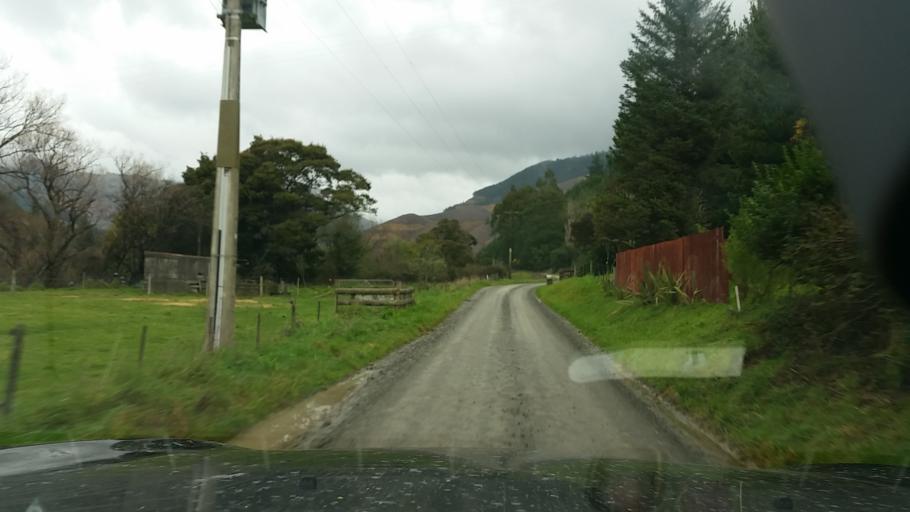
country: NZ
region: Marlborough
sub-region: Marlborough District
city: Picton
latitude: -41.2961
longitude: 173.6647
